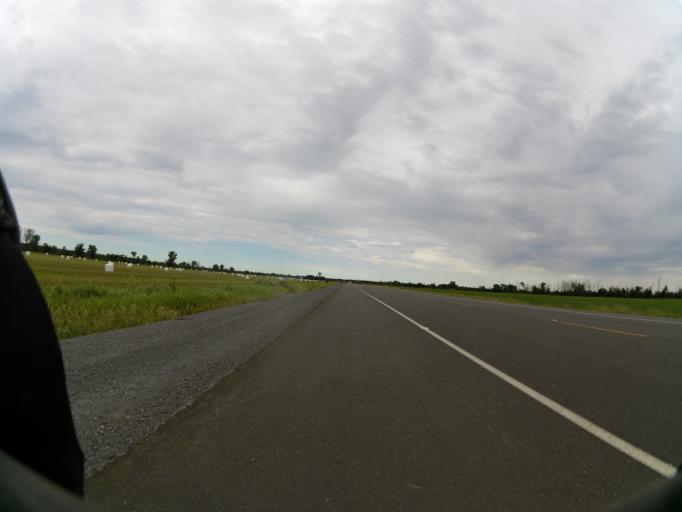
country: CA
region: Ontario
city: Bells Corners
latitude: 45.3034
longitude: -75.7208
